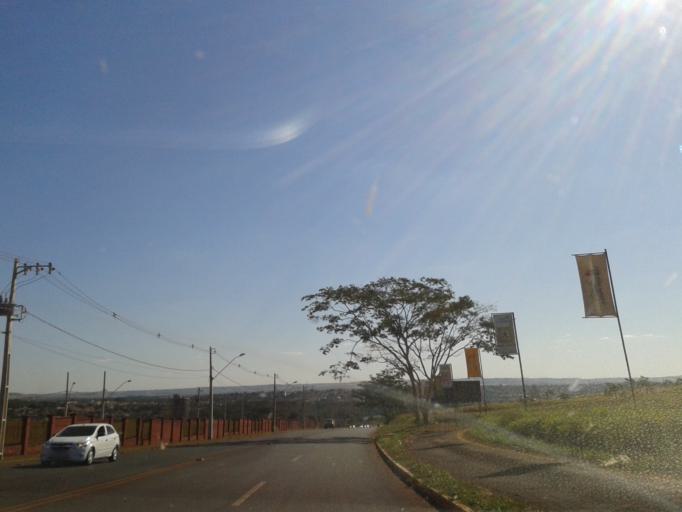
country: BR
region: Goias
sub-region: Itumbiara
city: Itumbiara
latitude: -18.4284
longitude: -49.1961
